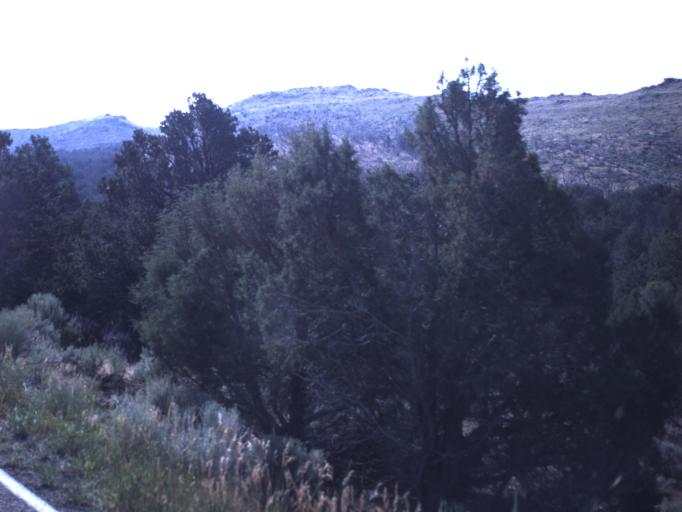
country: US
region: Utah
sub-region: Daggett County
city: Manila
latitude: 40.9526
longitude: -109.4641
